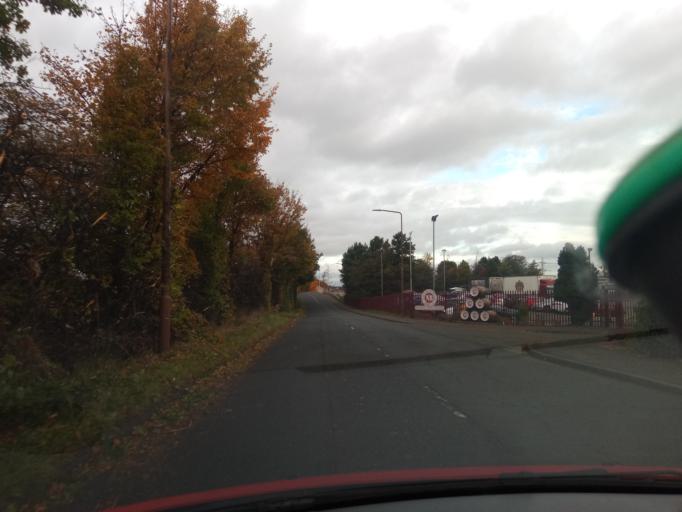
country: GB
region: Scotland
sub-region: West Lothian
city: Blackburn
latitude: 55.8399
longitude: -3.6134
